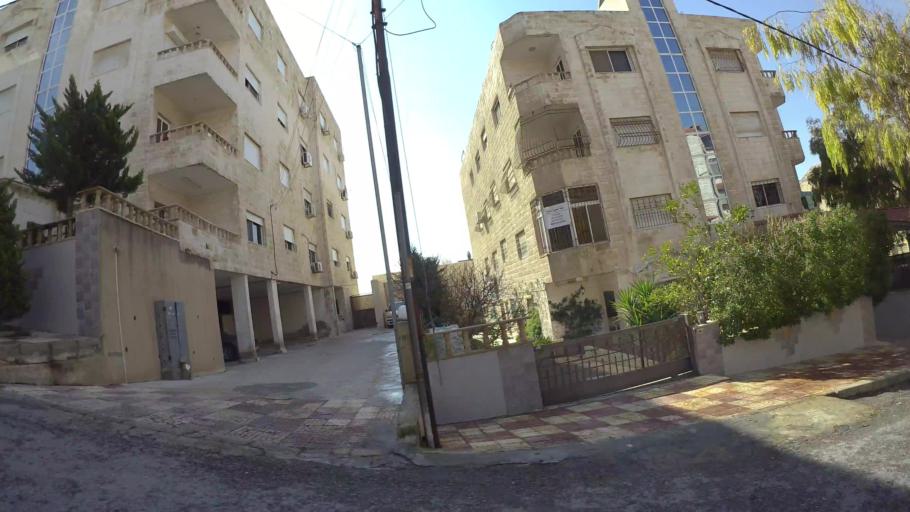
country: JO
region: Amman
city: Al Jubayhah
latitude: 31.9917
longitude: 35.8944
